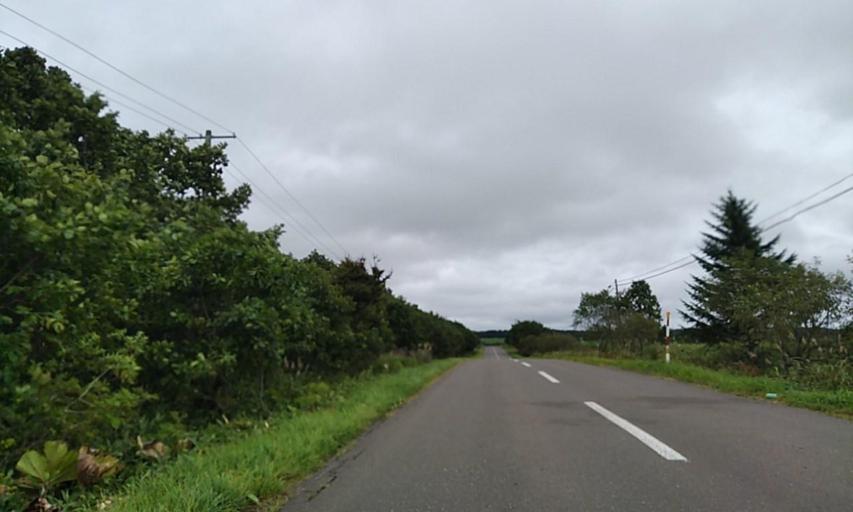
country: JP
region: Hokkaido
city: Nemuro
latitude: 43.2589
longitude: 145.2516
